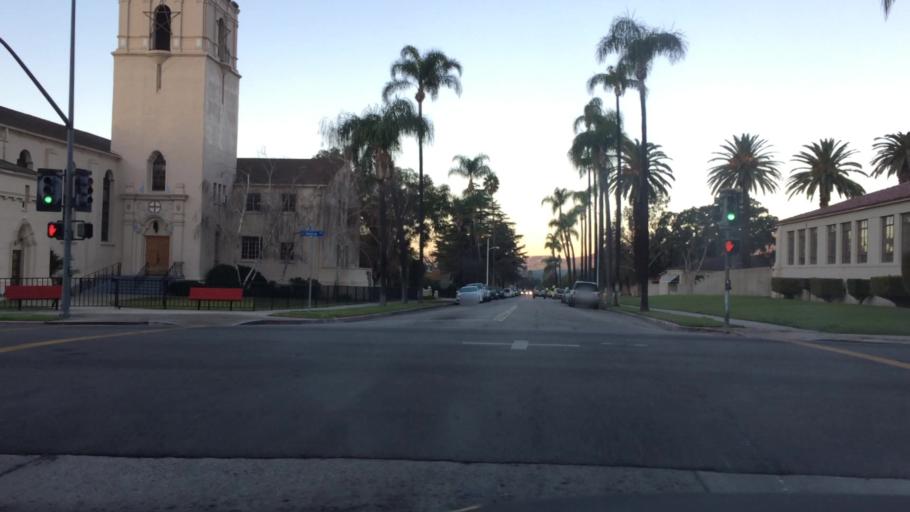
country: US
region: California
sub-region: Ventura County
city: Fillmore
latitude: 34.4026
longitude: -118.9141
